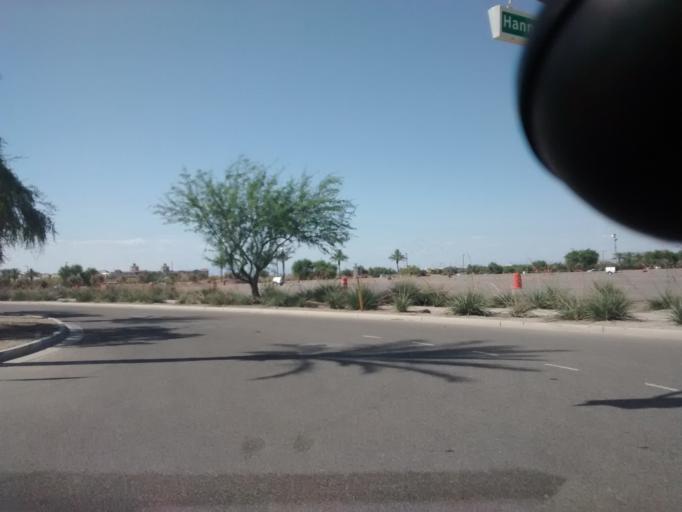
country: US
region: Arizona
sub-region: Maricopa County
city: Peoria
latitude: 33.5353
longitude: -112.2576
